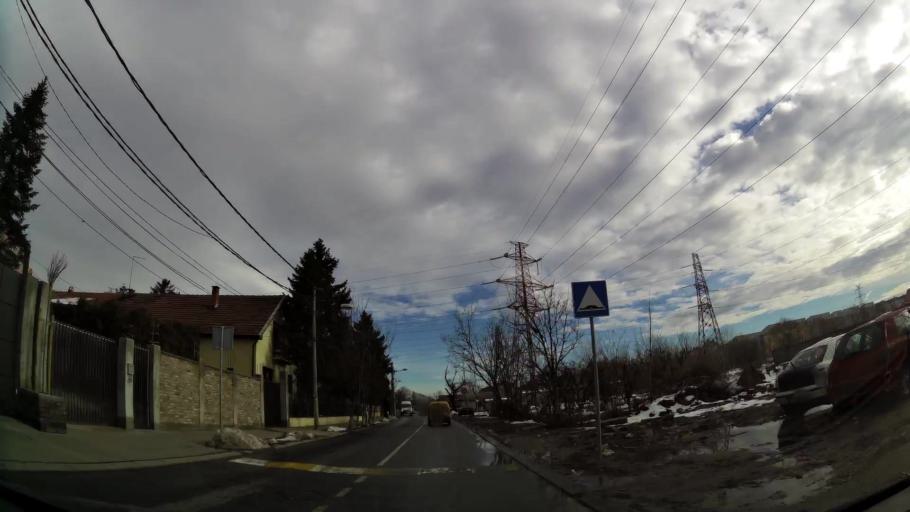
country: RS
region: Central Serbia
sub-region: Belgrade
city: Zemun
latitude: 44.8012
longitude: 20.3596
